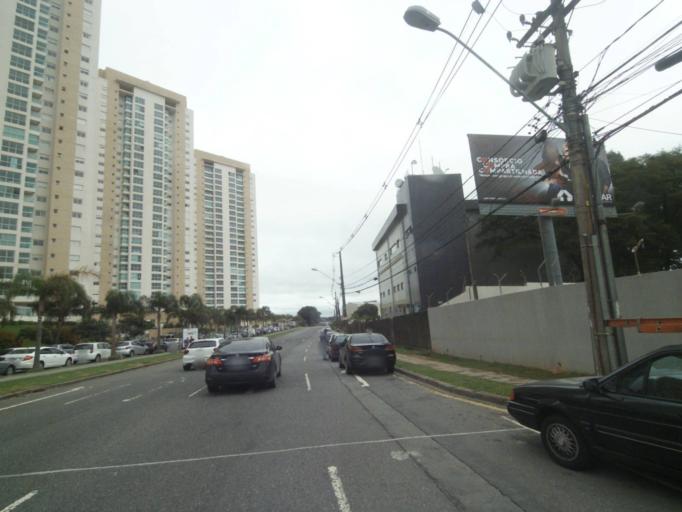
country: BR
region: Parana
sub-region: Curitiba
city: Curitiba
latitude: -25.4404
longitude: -49.3464
